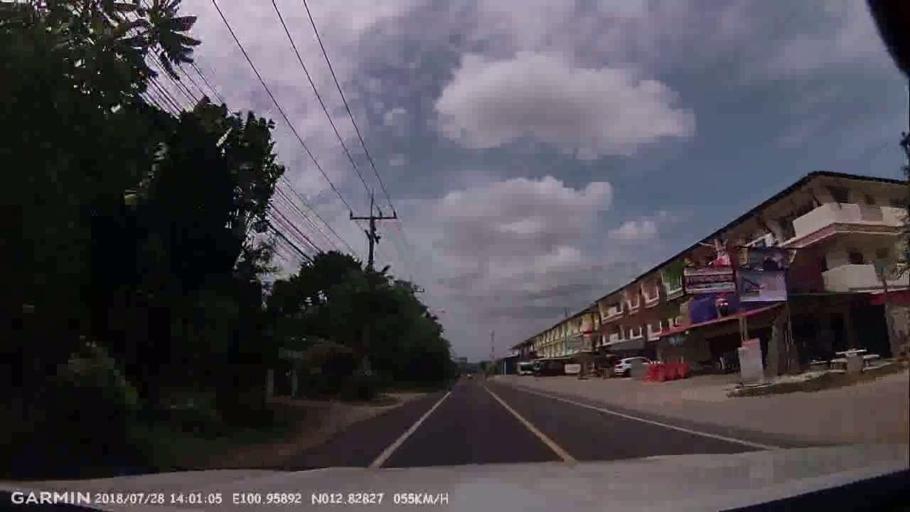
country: TH
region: Chon Buri
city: Phatthaya
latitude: 12.8283
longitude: 100.9591
